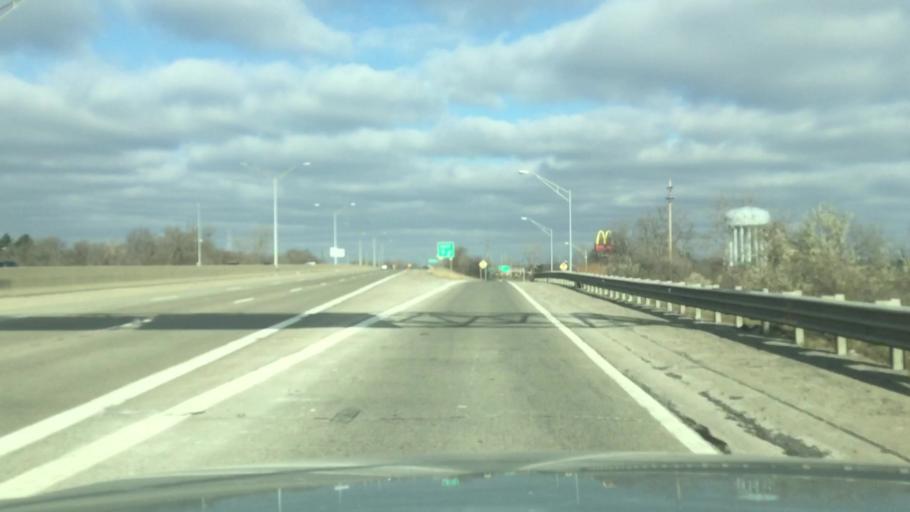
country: US
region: Michigan
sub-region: Genesee County
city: Flint
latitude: 43.0514
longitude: -83.6735
